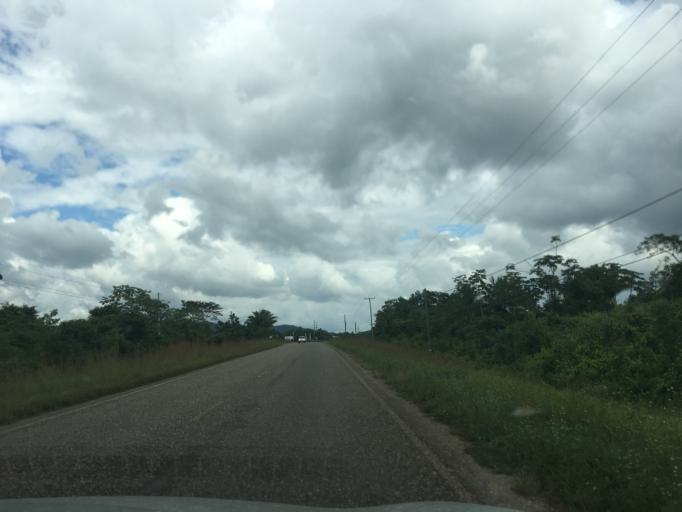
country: BZ
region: Stann Creek
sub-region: Dangriga
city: Dangriga
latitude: 16.9166
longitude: -88.3426
